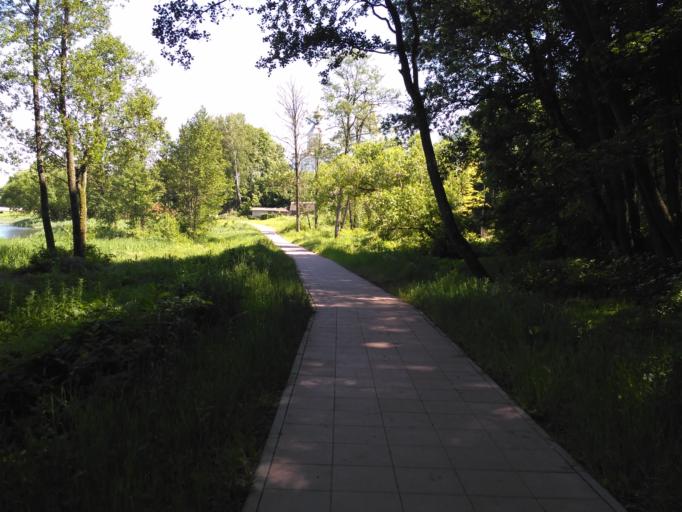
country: BY
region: Minsk
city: Lahoysk
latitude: 54.2032
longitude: 27.8484
